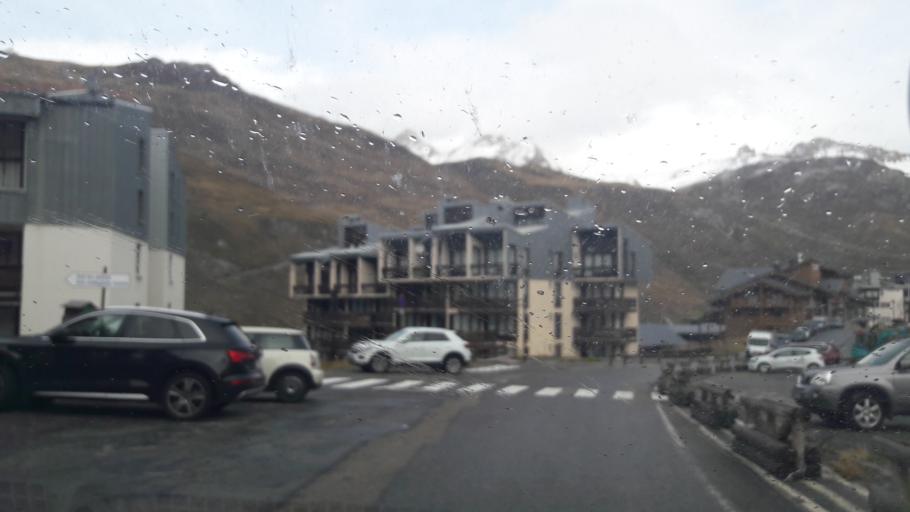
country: FR
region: Rhone-Alpes
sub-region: Departement de la Savoie
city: Tignes
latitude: 45.4540
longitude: 6.9001
